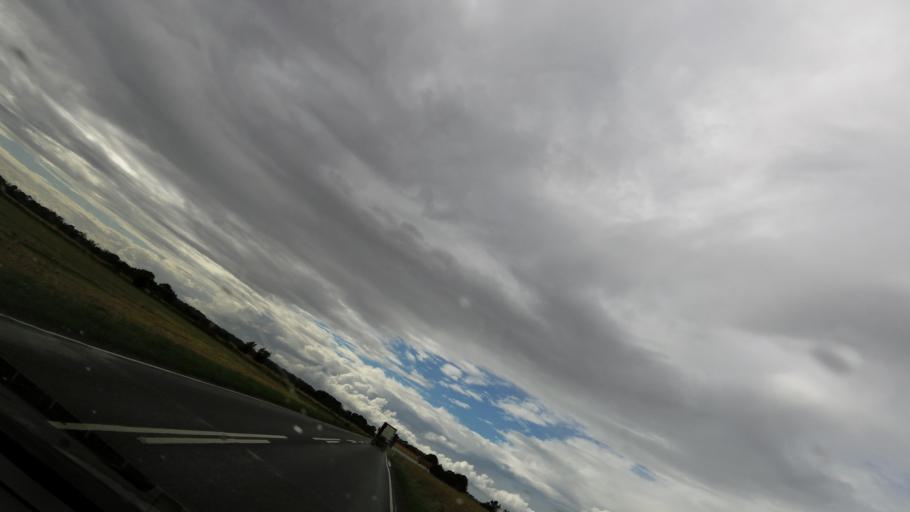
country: DK
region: South Denmark
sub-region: Nordfyns Kommune
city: Sonderso
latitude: 55.4887
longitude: 10.3082
